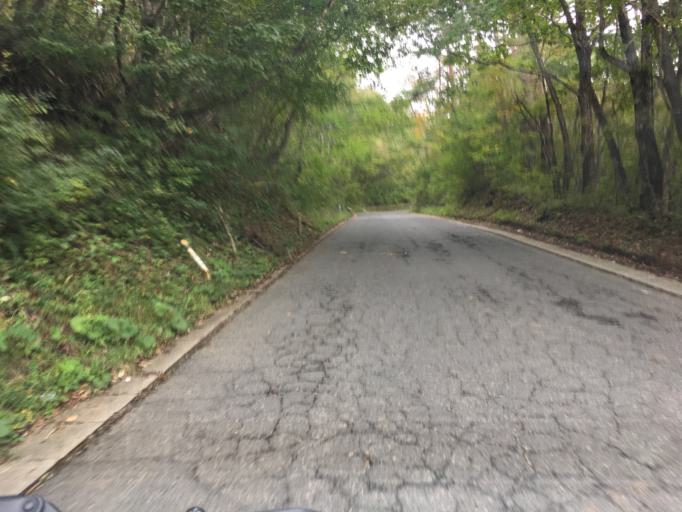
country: JP
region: Miyagi
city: Marumori
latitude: 37.8755
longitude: 140.6984
